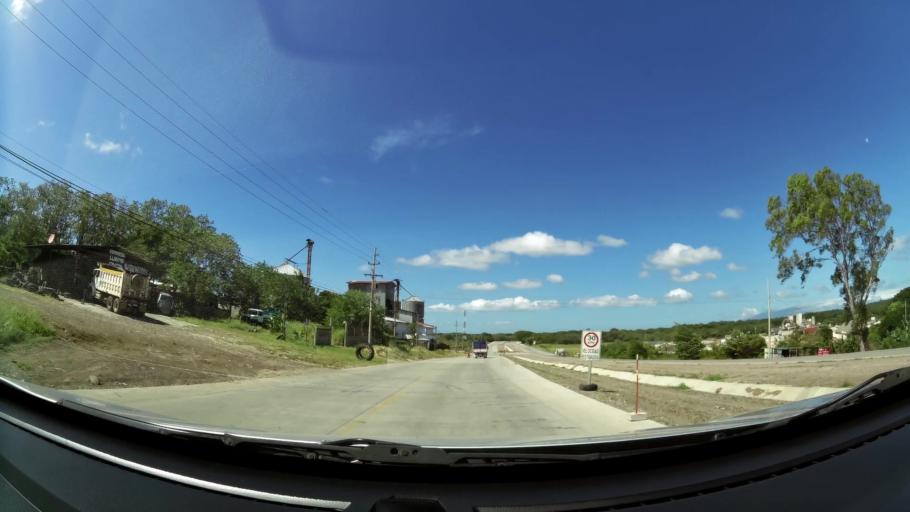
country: CR
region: Guanacaste
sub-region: Canton de Canas
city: Canas
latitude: 10.4476
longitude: -85.1218
